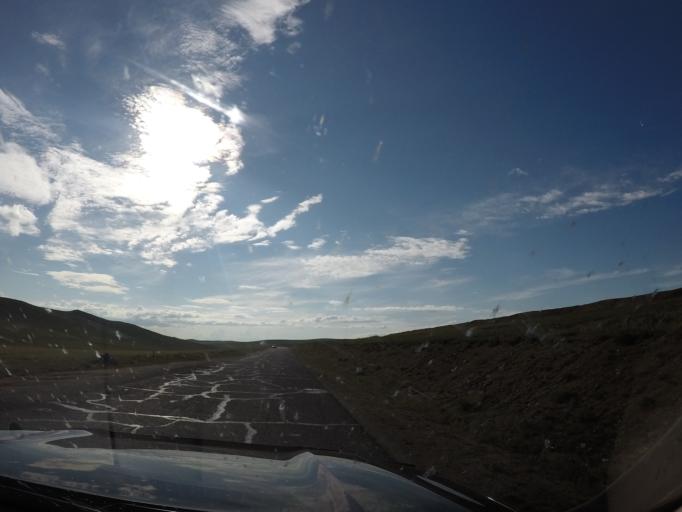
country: MN
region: Hentiy
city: Modot
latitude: 47.8055
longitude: 108.7248
